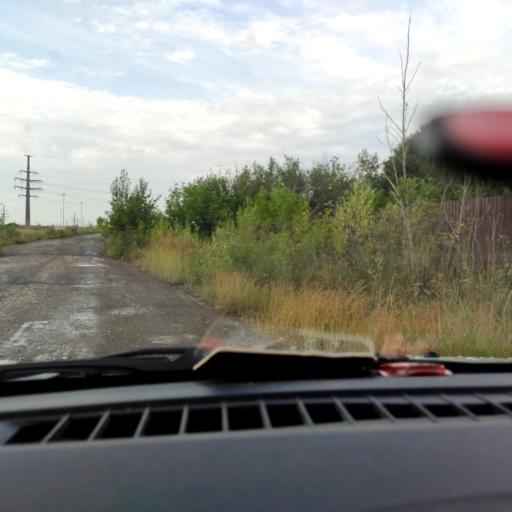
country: RU
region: Perm
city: Kondratovo
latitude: 57.9415
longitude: 56.1610
